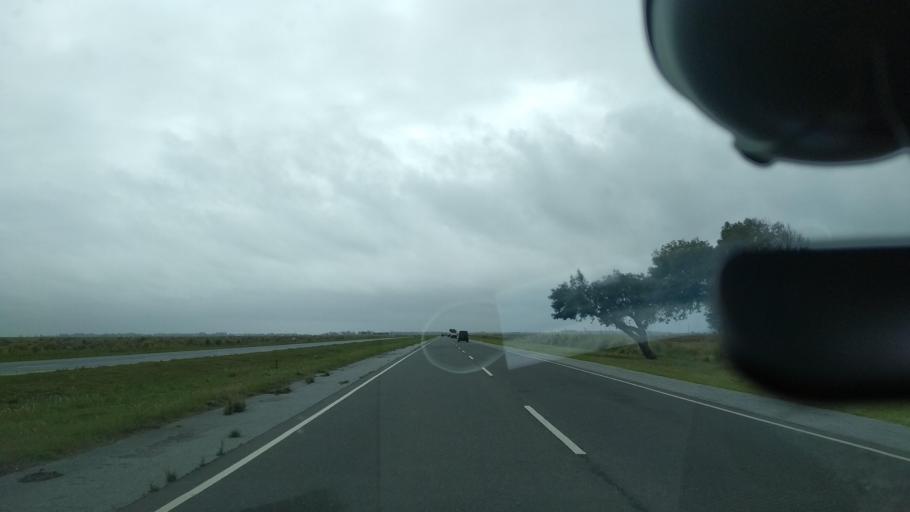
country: AR
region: Buenos Aires
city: San Clemente del Tuyu
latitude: -36.4320
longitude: -56.7153
